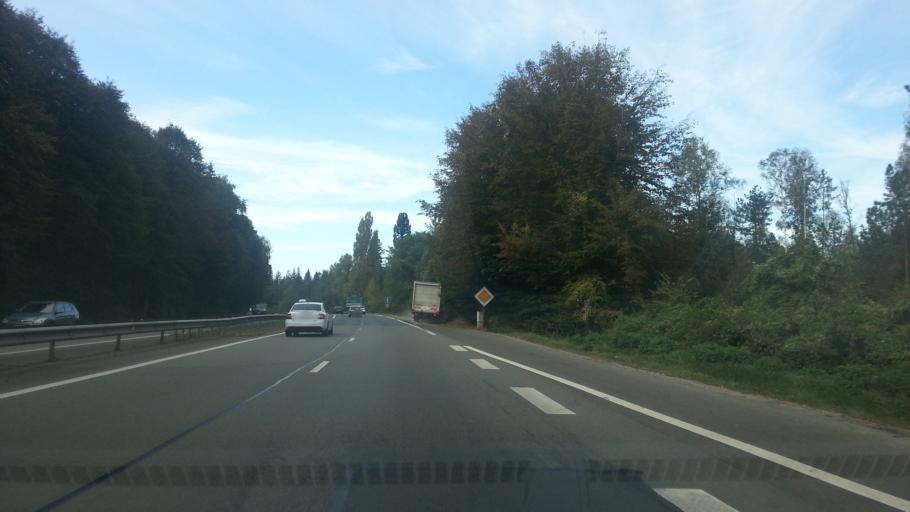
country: FR
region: Picardie
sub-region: Departement de l'Oise
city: Avilly-Saint-Leonard
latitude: 49.2342
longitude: 2.5355
